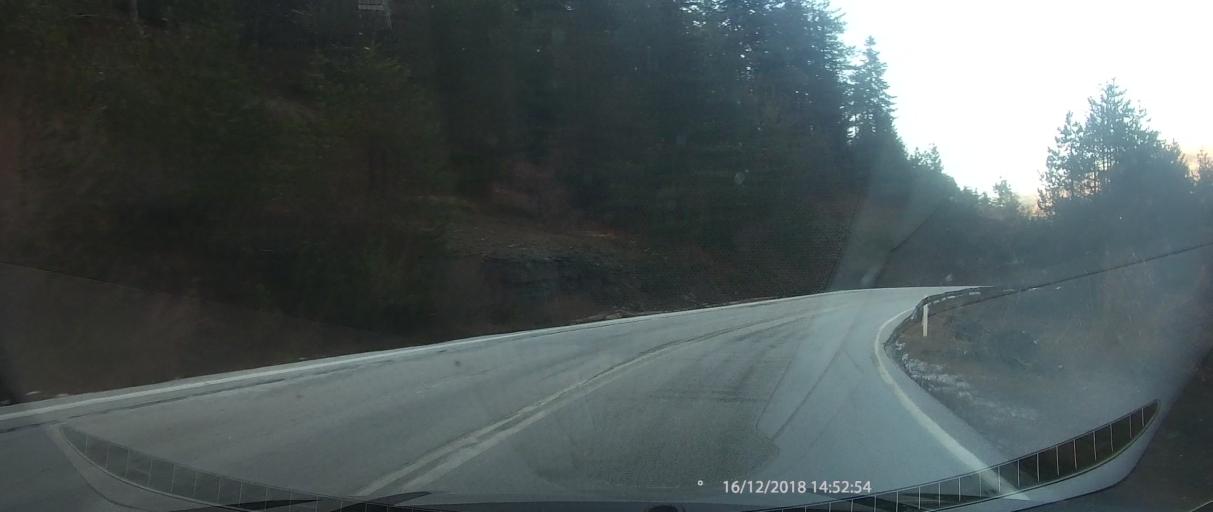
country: GR
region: West Macedonia
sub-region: Nomos Kastorias
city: Nestorio
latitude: 40.2062
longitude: 21.0583
